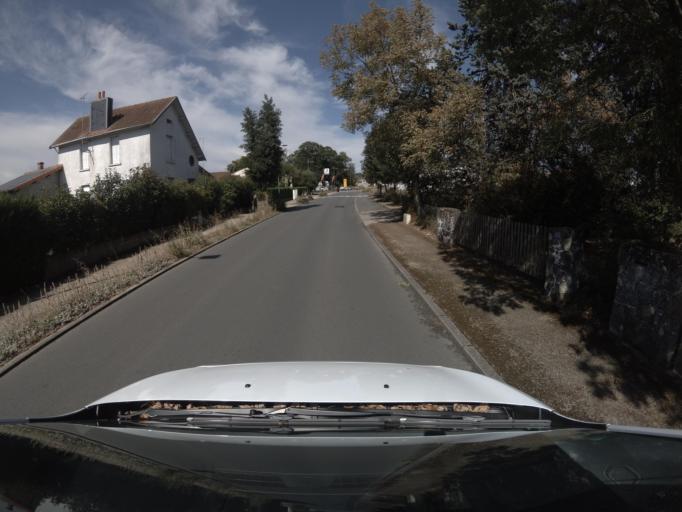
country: FR
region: Poitou-Charentes
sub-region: Departement des Deux-Sevres
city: Nueil-les-Aubiers
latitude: 46.9502
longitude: -0.5933
